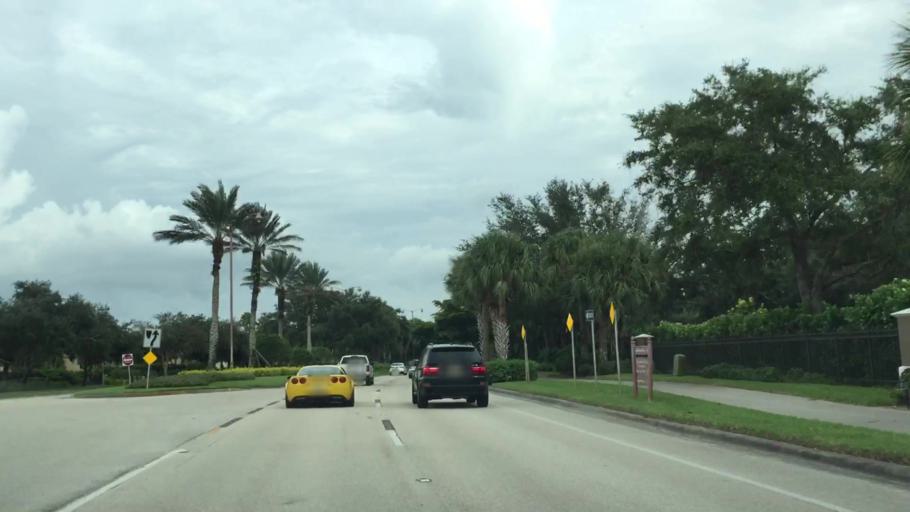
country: US
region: Florida
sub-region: Lee County
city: Estero
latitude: 26.3987
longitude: -81.7990
